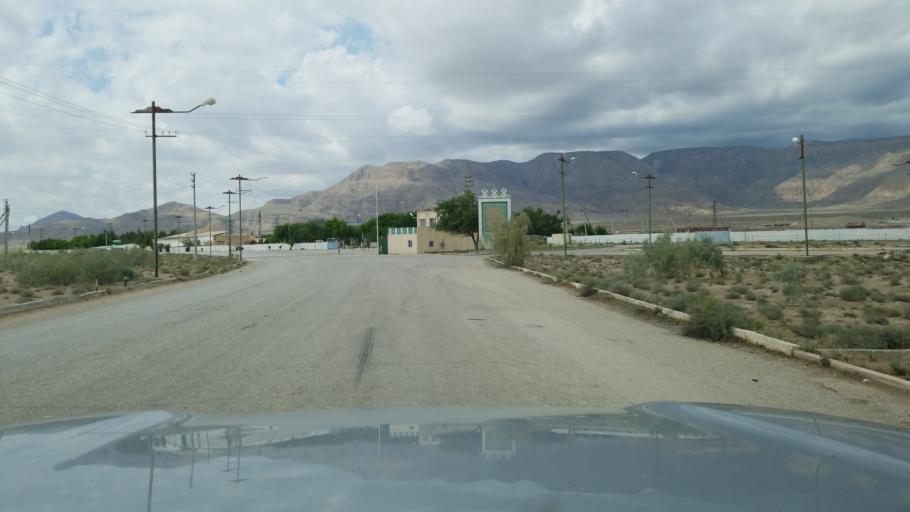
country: TM
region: Balkan
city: Balkanabat
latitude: 39.4780
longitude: 54.4599
